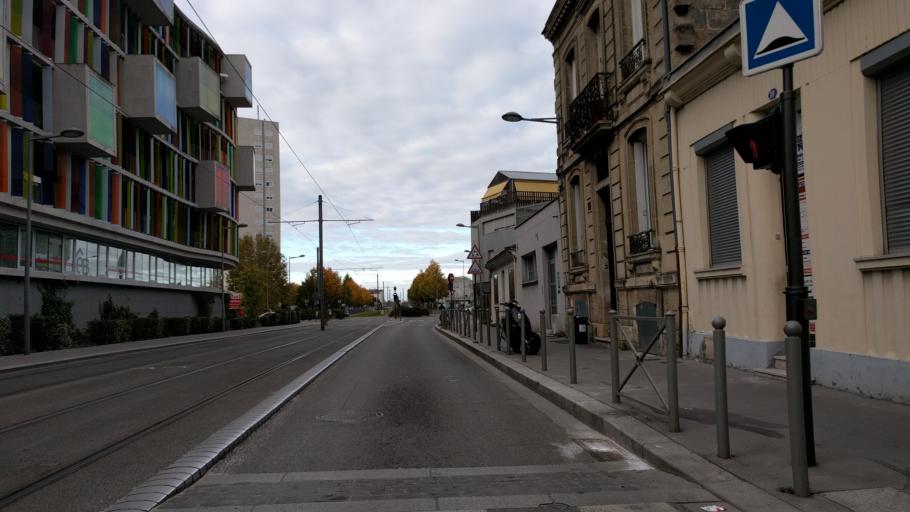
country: FR
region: Aquitaine
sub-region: Departement de la Gironde
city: Le Bouscat
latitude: 44.8599
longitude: -0.5750
